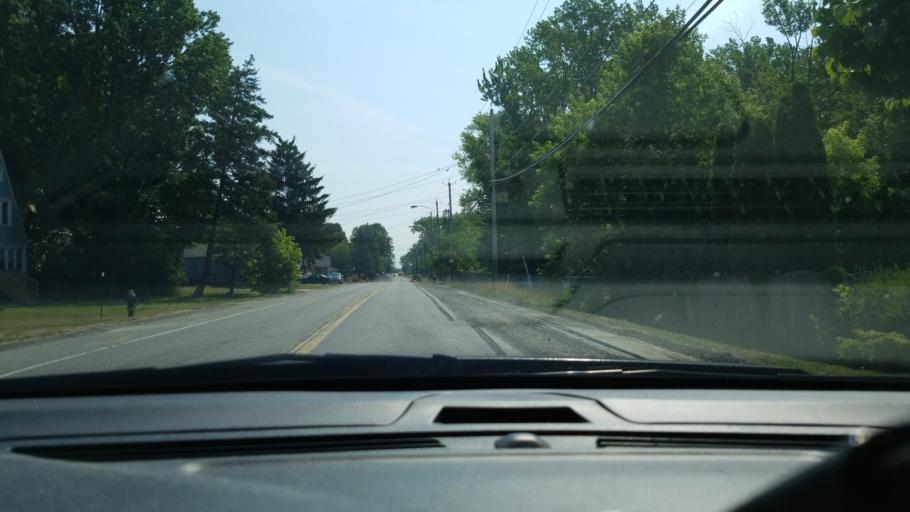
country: US
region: New York
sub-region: Onondaga County
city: Mattydale
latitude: 43.0984
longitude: -76.1325
